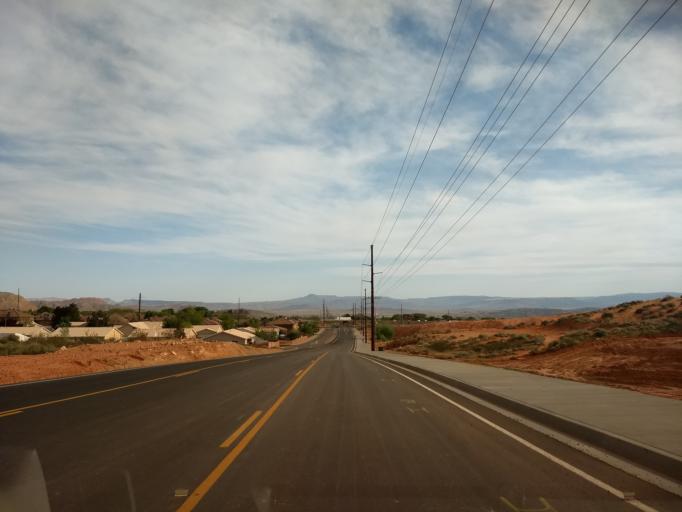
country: US
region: Utah
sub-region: Washington County
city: Washington
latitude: 37.1440
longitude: -113.5098
